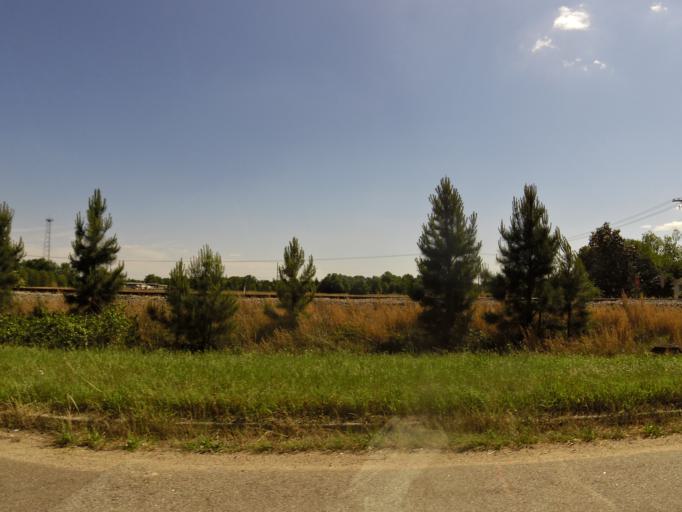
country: US
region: South Carolina
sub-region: Aiken County
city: Aiken
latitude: 33.5438
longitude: -81.6741
